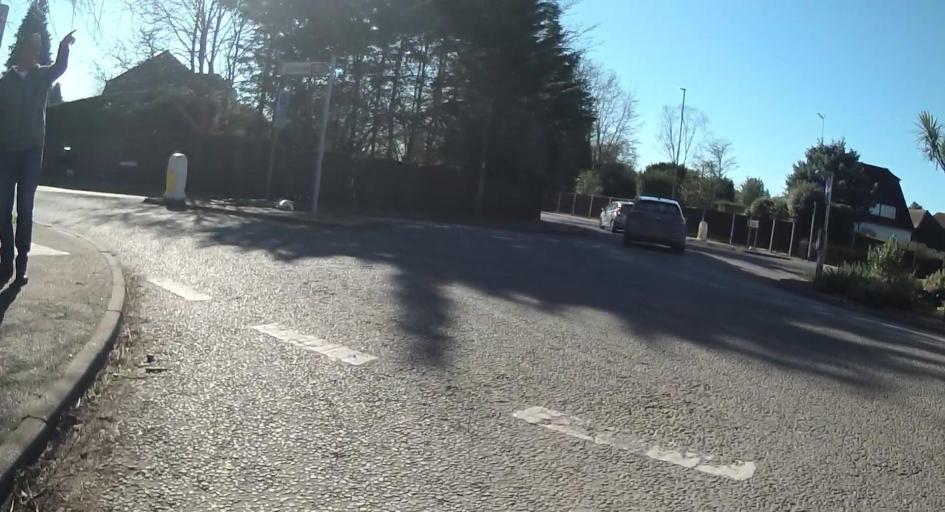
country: GB
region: England
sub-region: Surrey
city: Walton-on-Thames
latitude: 51.3796
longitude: -0.4188
